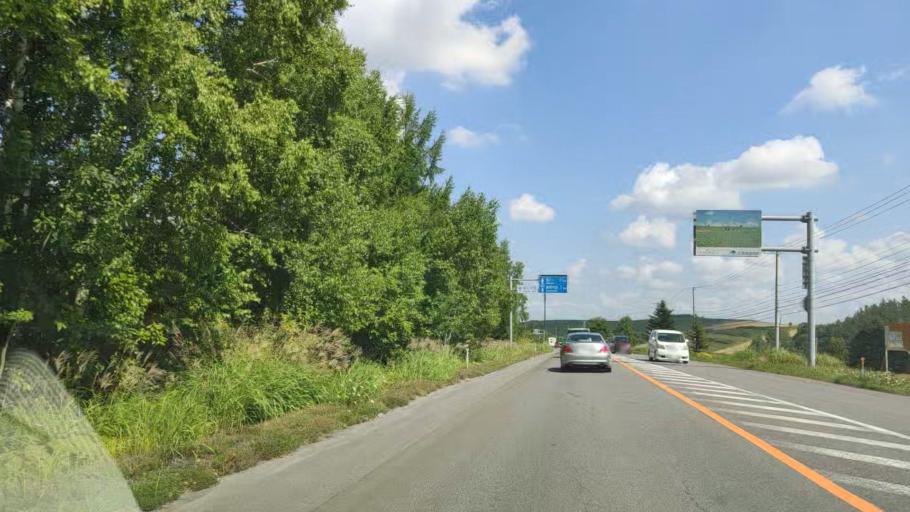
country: JP
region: Hokkaido
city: Shimo-furano
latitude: 43.5459
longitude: 142.4387
